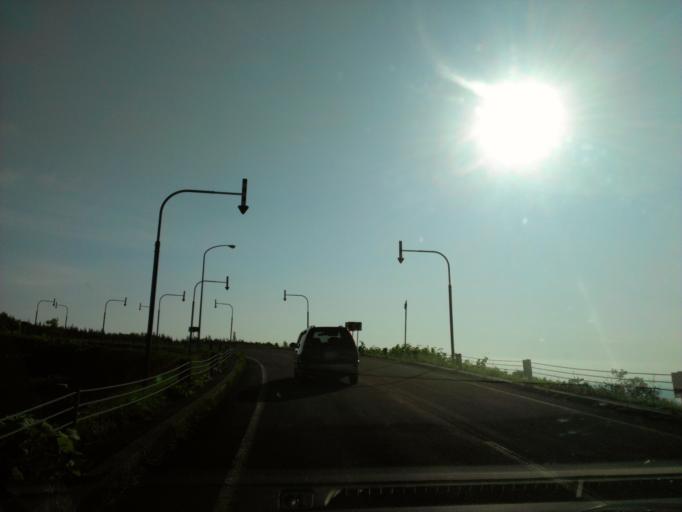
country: JP
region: Hokkaido
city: Shimo-furano
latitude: 43.4591
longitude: 142.6461
